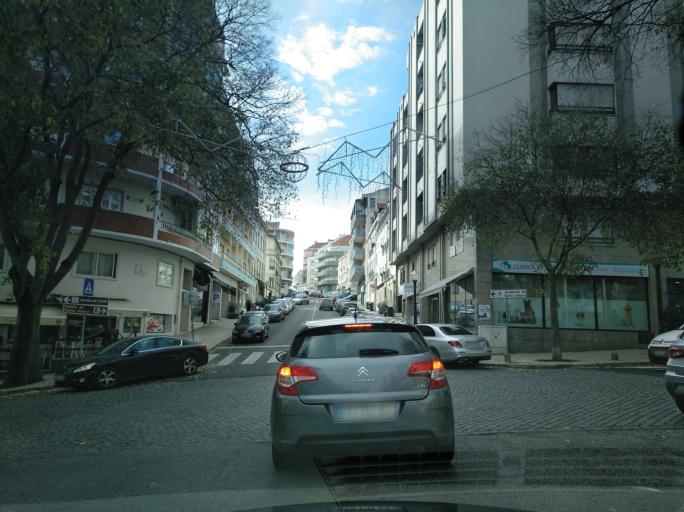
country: PT
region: Setubal
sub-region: Almada
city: Pragal
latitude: 38.7041
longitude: -9.1824
